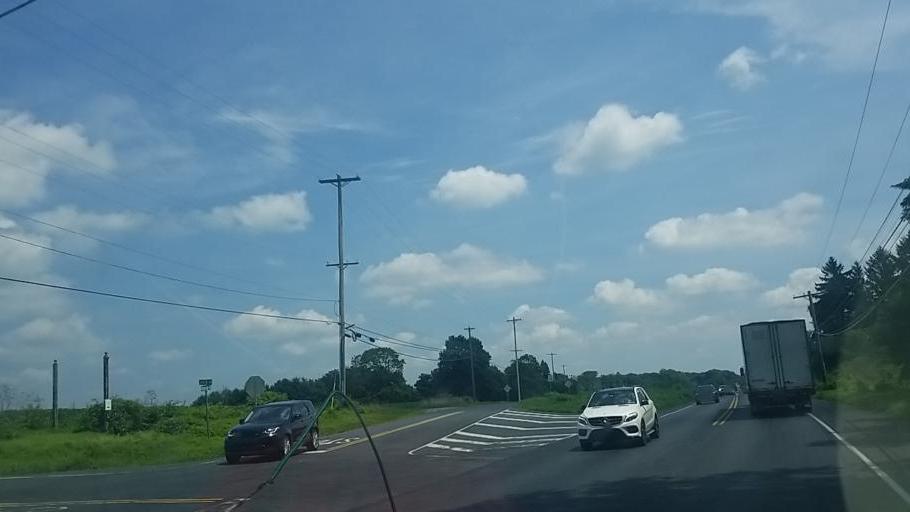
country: US
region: Pennsylvania
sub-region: Chester County
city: Toughkenamon
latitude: 39.8016
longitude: -75.7374
